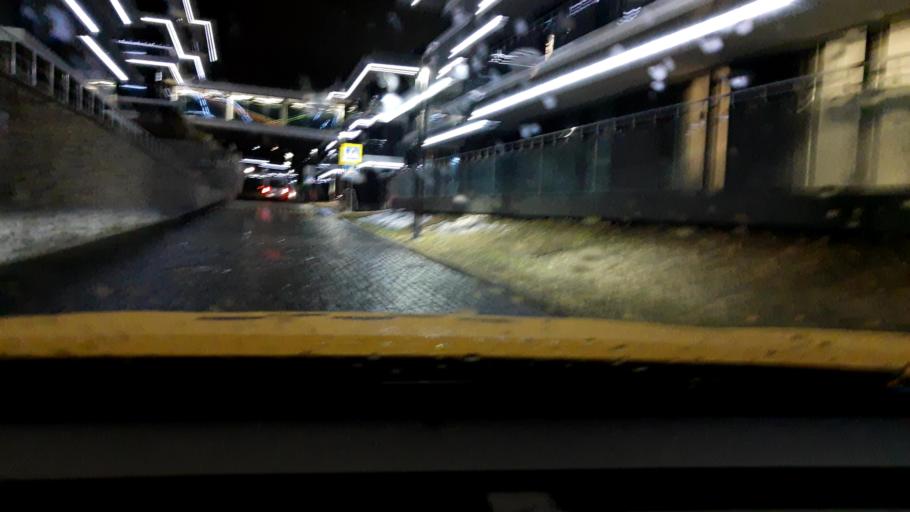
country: RU
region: Moskovskaya
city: Rozhdestveno
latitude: 55.8451
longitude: 37.0078
